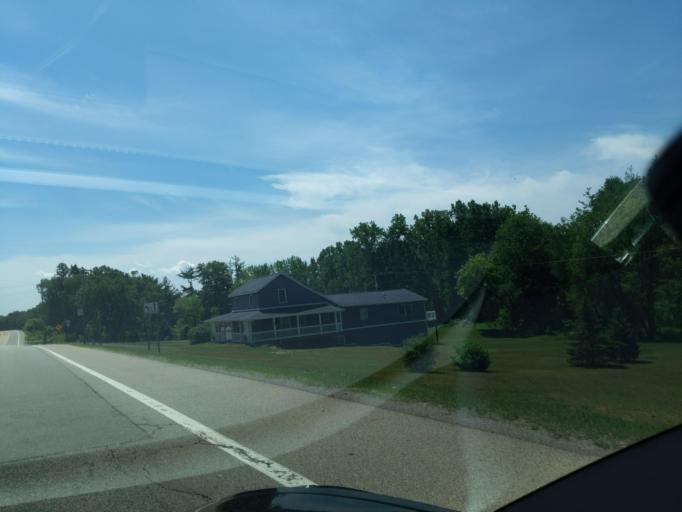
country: US
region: Michigan
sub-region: Kent County
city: Forest Hills
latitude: 42.9465
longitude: -85.4591
